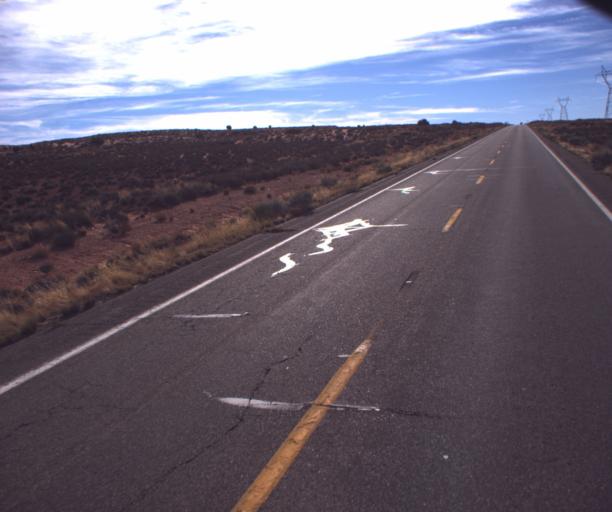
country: US
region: Arizona
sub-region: Coconino County
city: LeChee
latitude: 36.8550
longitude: -111.3361
